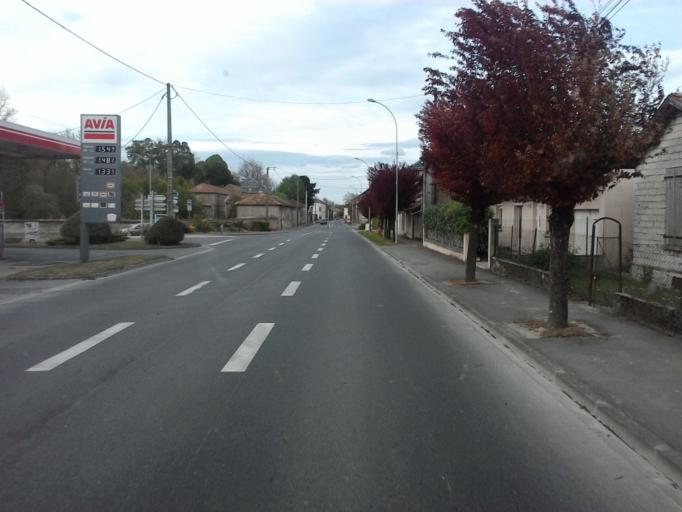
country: FR
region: Champagne-Ardenne
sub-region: Departement de la Marne
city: Suippes
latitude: 49.1279
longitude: 4.5258
